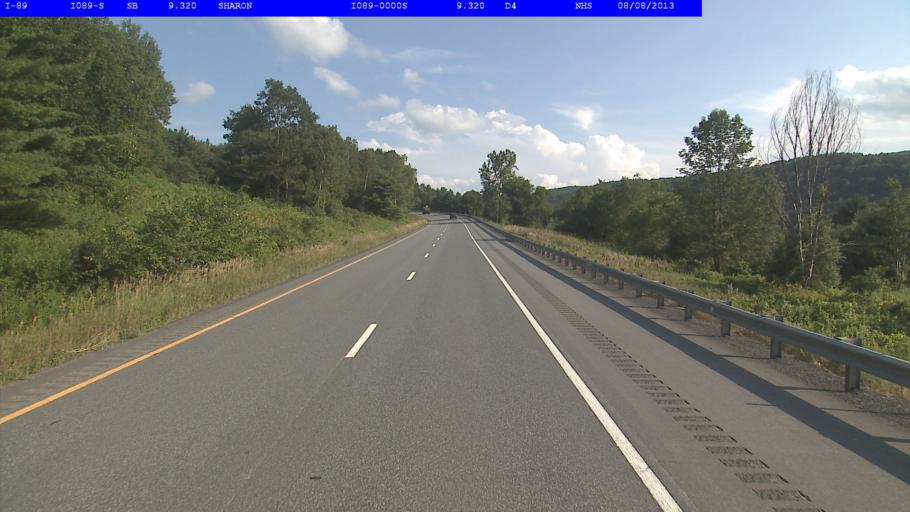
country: US
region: Vermont
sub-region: Windsor County
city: Wilder
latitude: 43.7325
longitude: -72.4323
